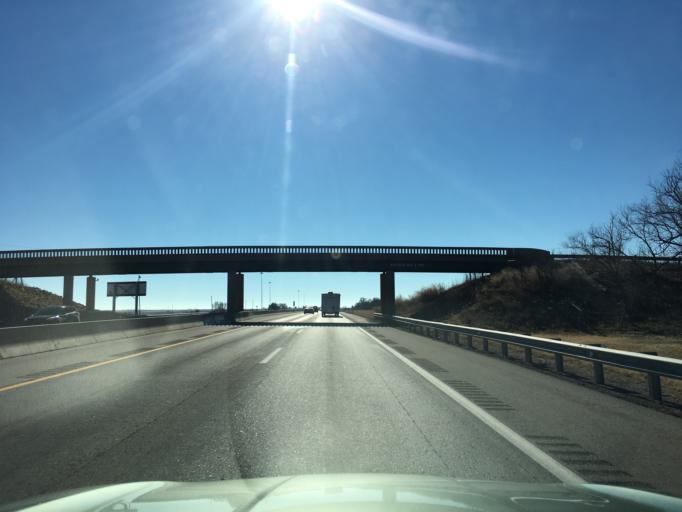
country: US
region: Oklahoma
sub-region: Kay County
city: Blackwell
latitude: 37.0290
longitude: -97.3383
